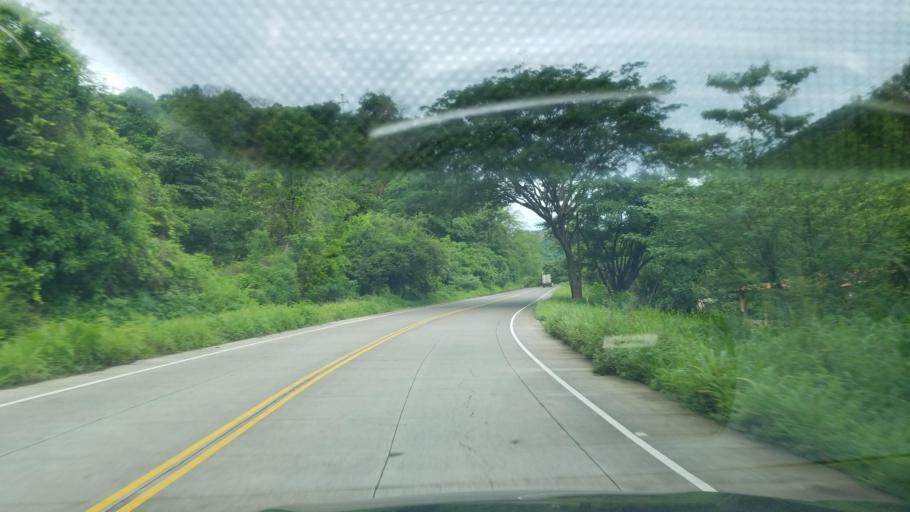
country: HN
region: Francisco Morazan
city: El Porvenir
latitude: 13.6858
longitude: -87.3467
